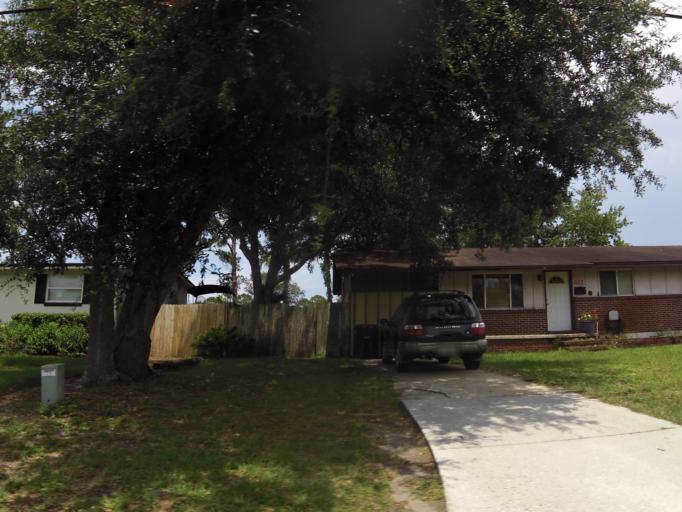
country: US
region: Florida
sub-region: Duval County
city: Atlantic Beach
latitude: 30.3296
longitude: -81.4075
